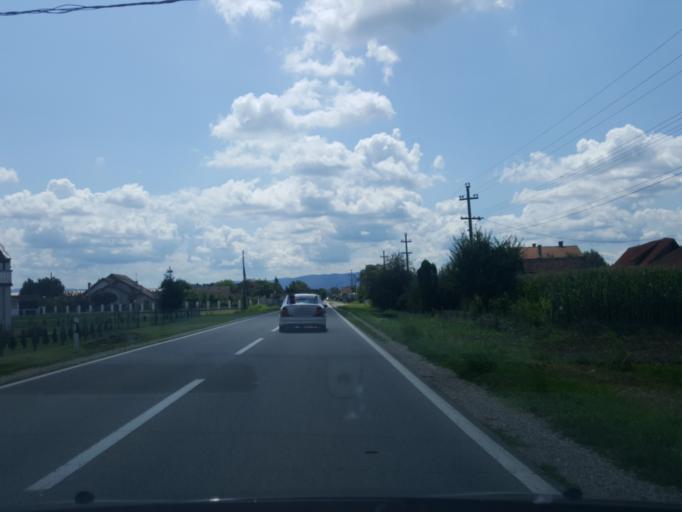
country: RS
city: Kozjak
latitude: 44.6237
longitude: 19.2691
